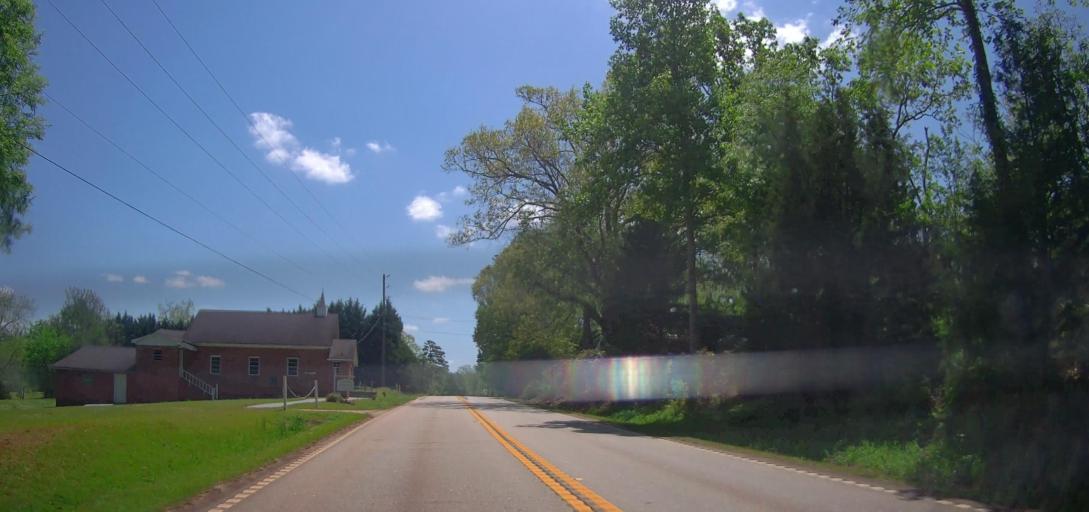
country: US
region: Georgia
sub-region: Jasper County
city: Monticello
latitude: 33.1854
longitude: -83.6444
